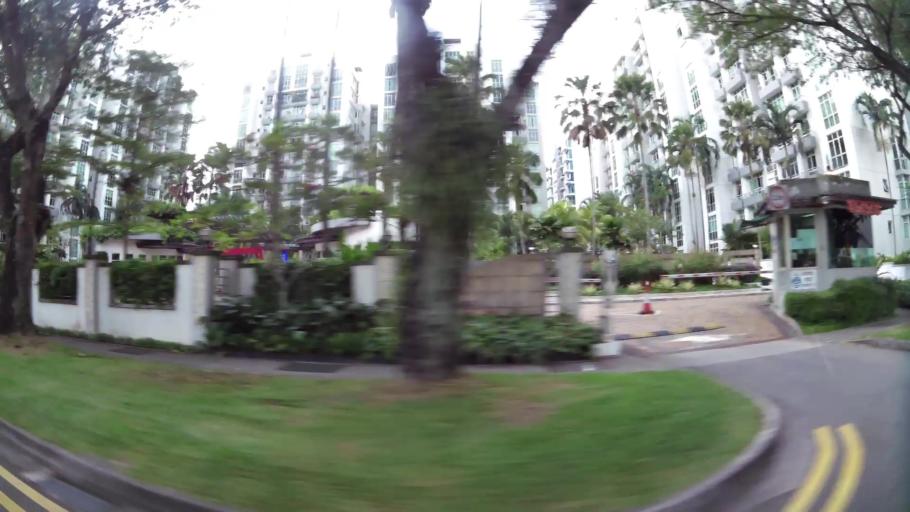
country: MY
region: Johor
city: Kampung Pasir Gudang Baru
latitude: 1.4246
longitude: 103.8495
